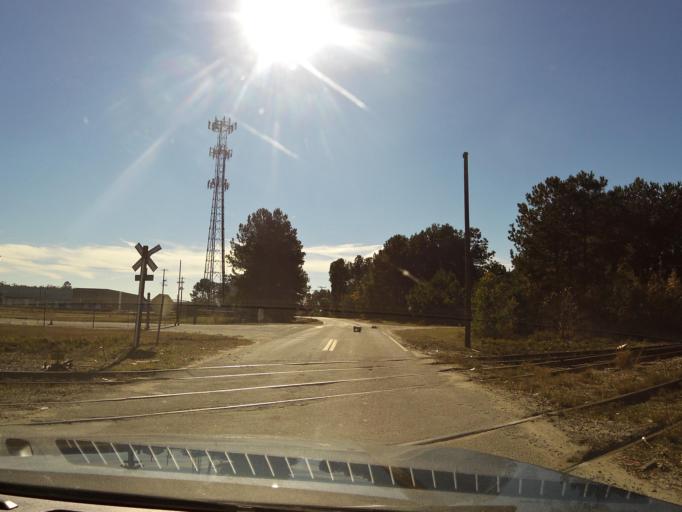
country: US
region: Georgia
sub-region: Chatham County
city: Savannah
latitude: 32.0698
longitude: -81.1420
